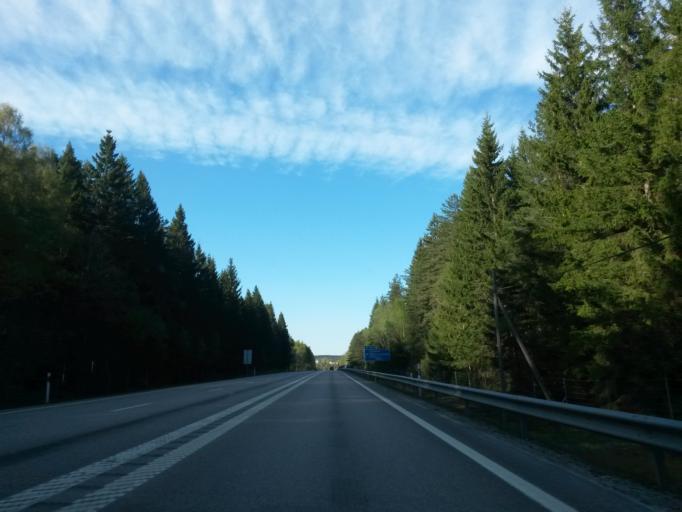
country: SE
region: Vaestra Goetaland
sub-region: Vargarda Kommun
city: Vargarda
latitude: 58.0168
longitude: 12.7777
